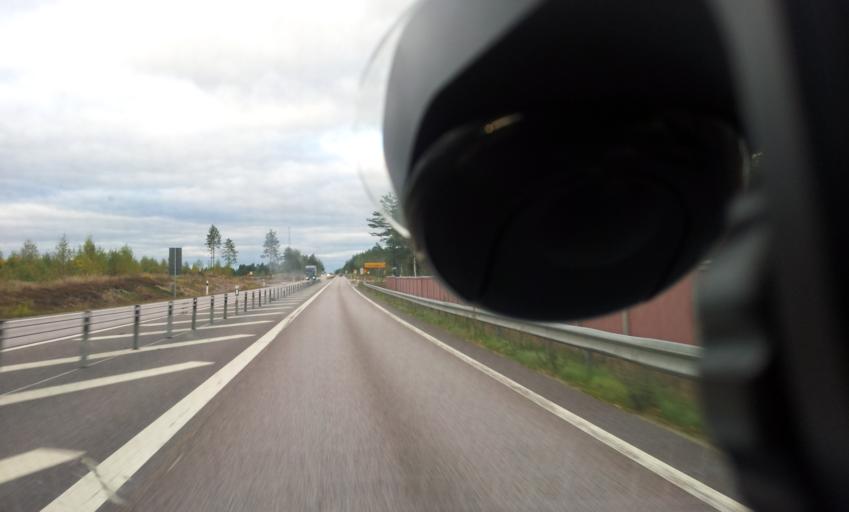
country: SE
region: Kalmar
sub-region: Oskarshamns Kommun
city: Oskarshamn
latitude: 57.3967
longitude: 16.4785
